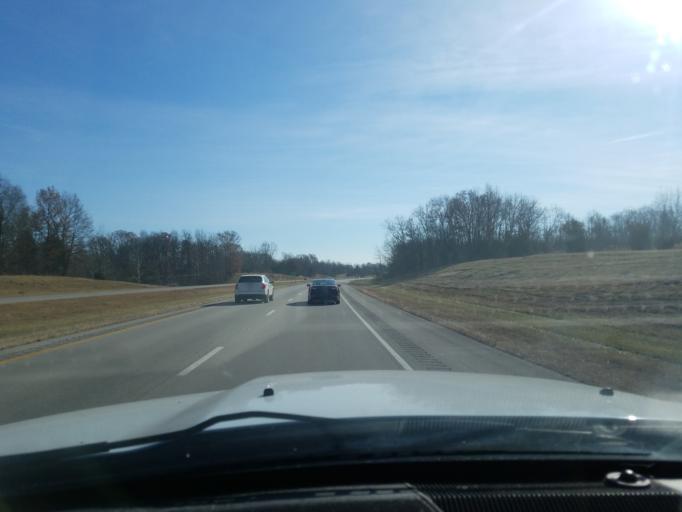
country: US
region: Ohio
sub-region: Adams County
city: Winchester
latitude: 38.9482
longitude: -83.6811
